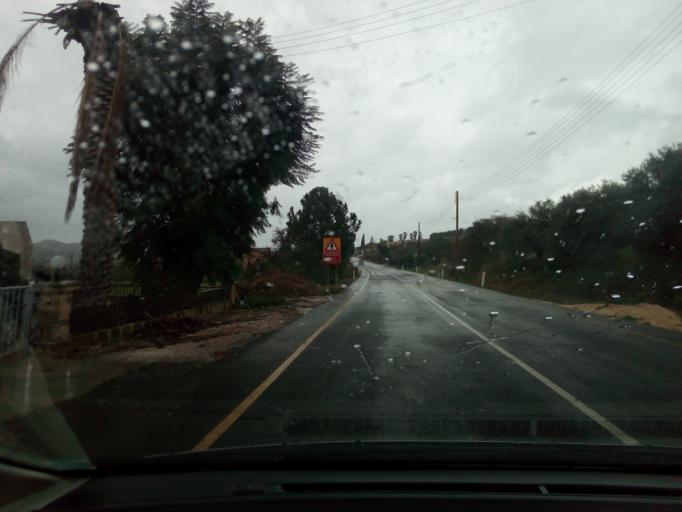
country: CY
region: Pafos
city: Polis
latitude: 34.9942
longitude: 32.4485
